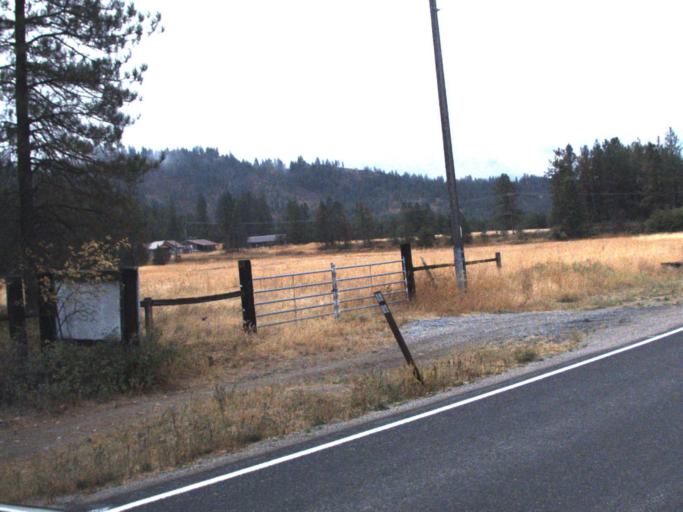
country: US
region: Washington
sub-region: Stevens County
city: Chewelah
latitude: 48.0503
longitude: -117.7415
